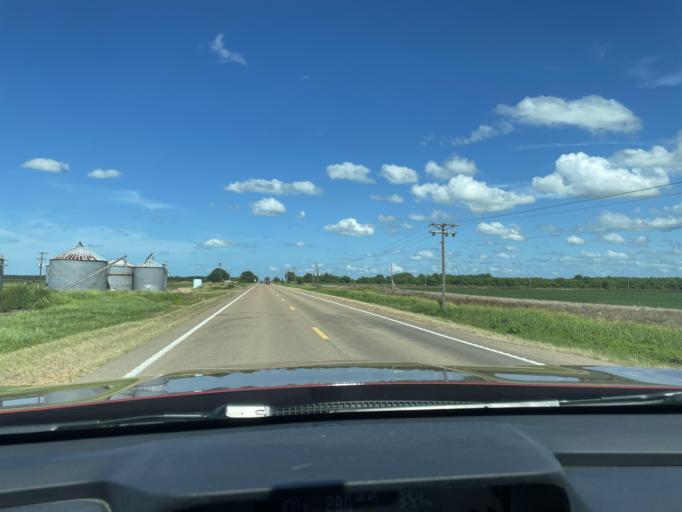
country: US
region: Mississippi
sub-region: Humphreys County
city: Belzoni
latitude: 33.1829
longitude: -90.6513
